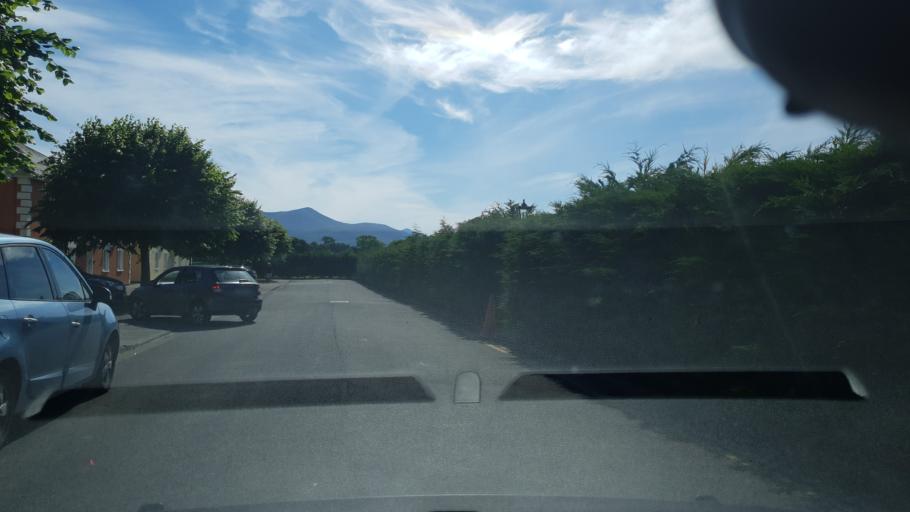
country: IE
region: Munster
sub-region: Ciarrai
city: Cill Airne
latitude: 52.0569
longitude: -9.4937
